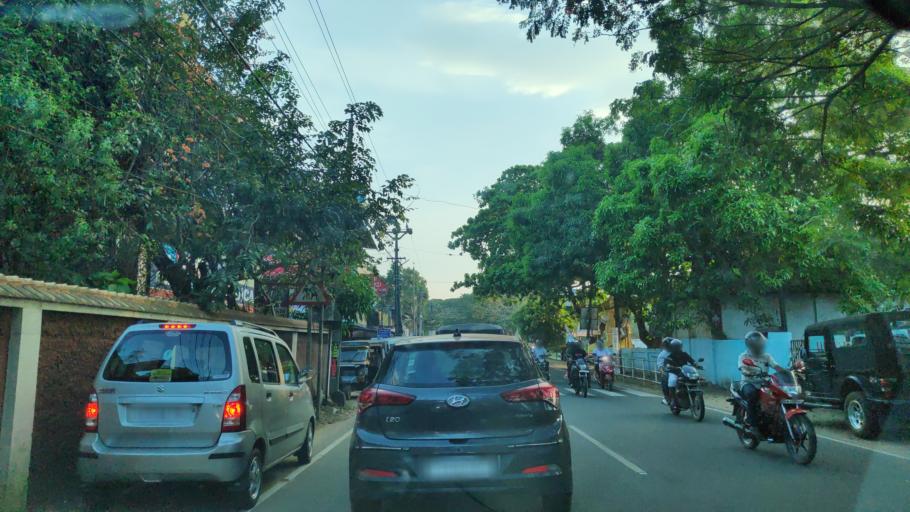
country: IN
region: Kerala
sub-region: Alappuzha
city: Shertallai
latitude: 9.6817
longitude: 76.3422
